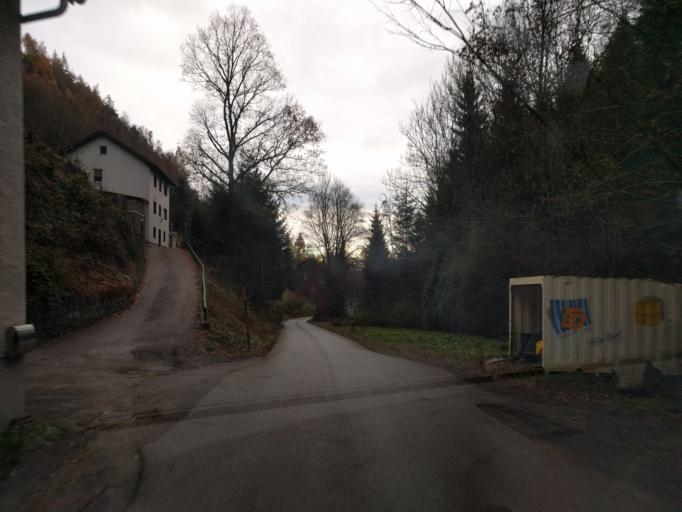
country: AT
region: Upper Austria
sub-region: Politischer Bezirk Urfahr-Umgebung
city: Kirchschlag bei Linz
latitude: 48.4091
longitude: 14.2960
